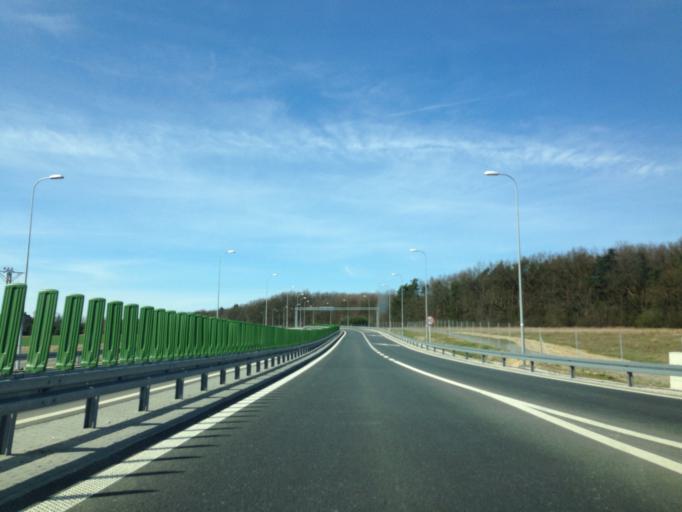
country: PL
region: Lodz Voivodeship
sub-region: Powiat zdunskowolski
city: Zapolice
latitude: 51.5939
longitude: 18.8229
